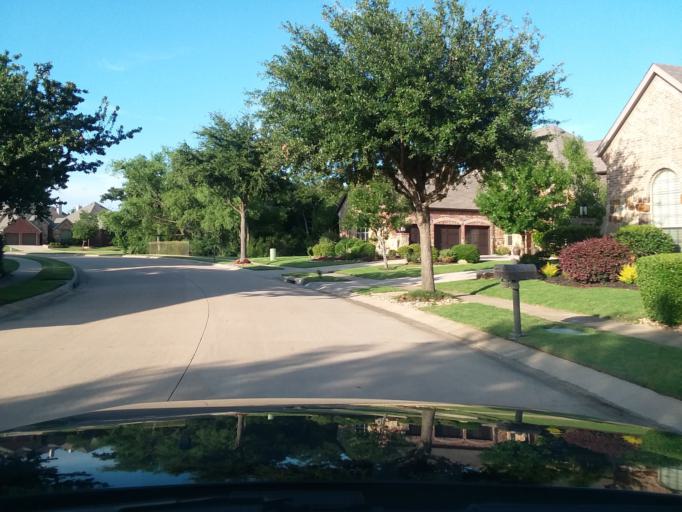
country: US
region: Texas
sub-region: Denton County
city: Copper Canyon
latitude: 33.1042
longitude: -97.1212
